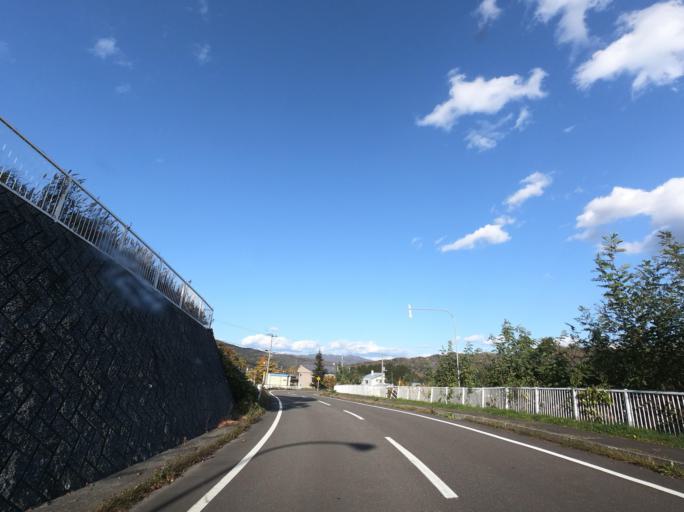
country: JP
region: Hokkaido
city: Iwamizawa
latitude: 42.9846
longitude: 142.0031
